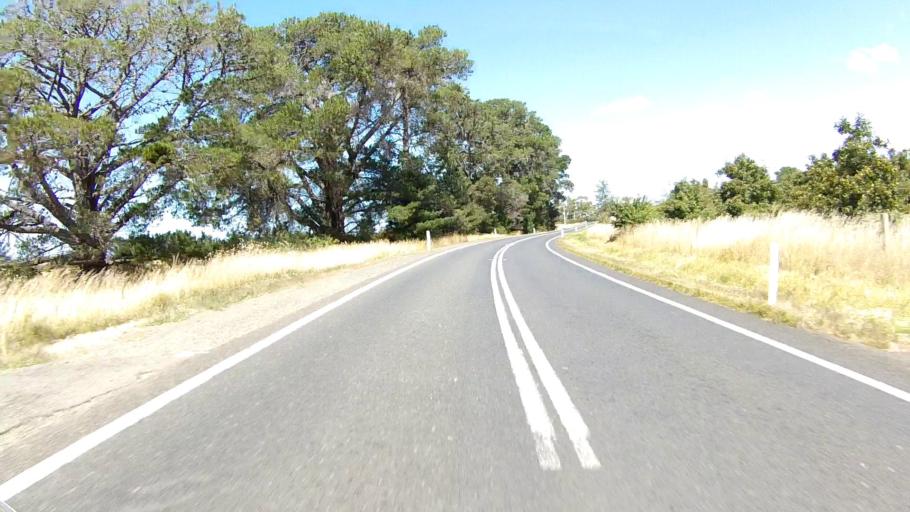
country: AU
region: Tasmania
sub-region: Break O'Day
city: St Helens
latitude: -42.0647
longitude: 148.0636
